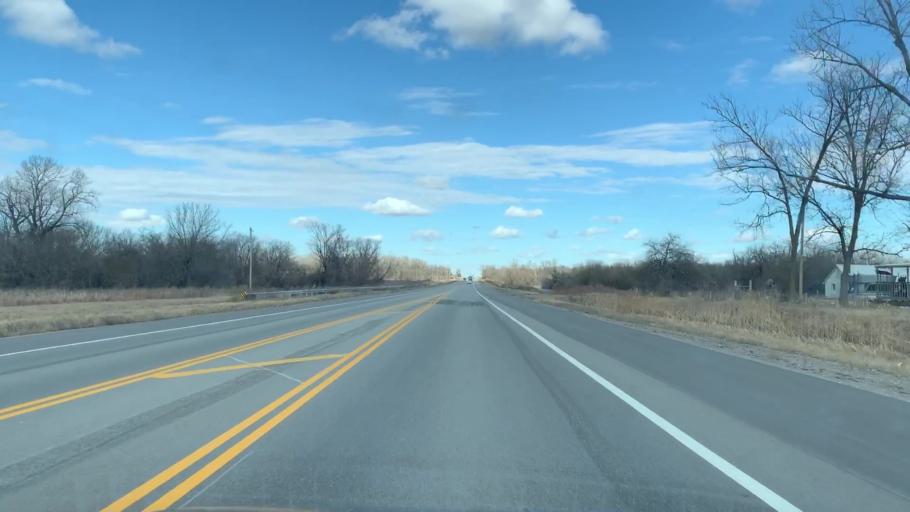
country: US
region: Kansas
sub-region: Cherokee County
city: Columbus
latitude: 37.3133
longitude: -94.8322
